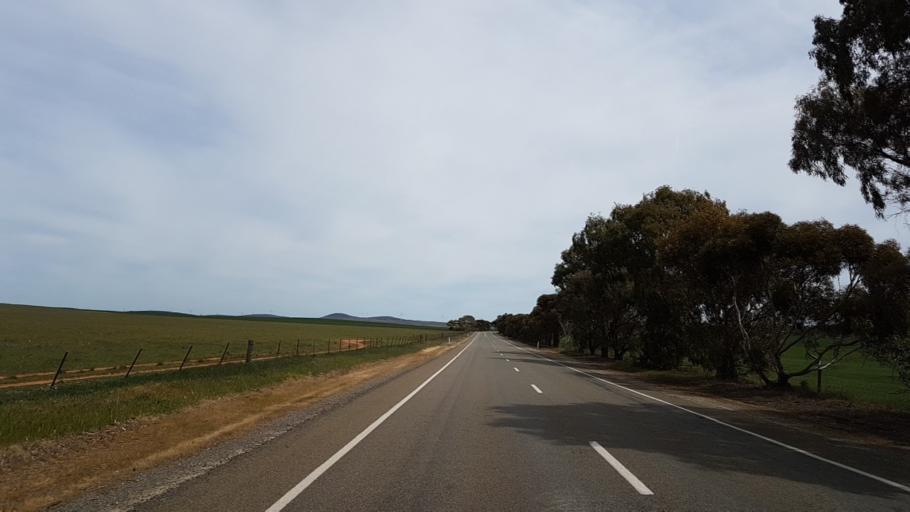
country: AU
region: South Australia
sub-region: Northern Areas
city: Jamestown
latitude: -33.0331
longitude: 138.6571
